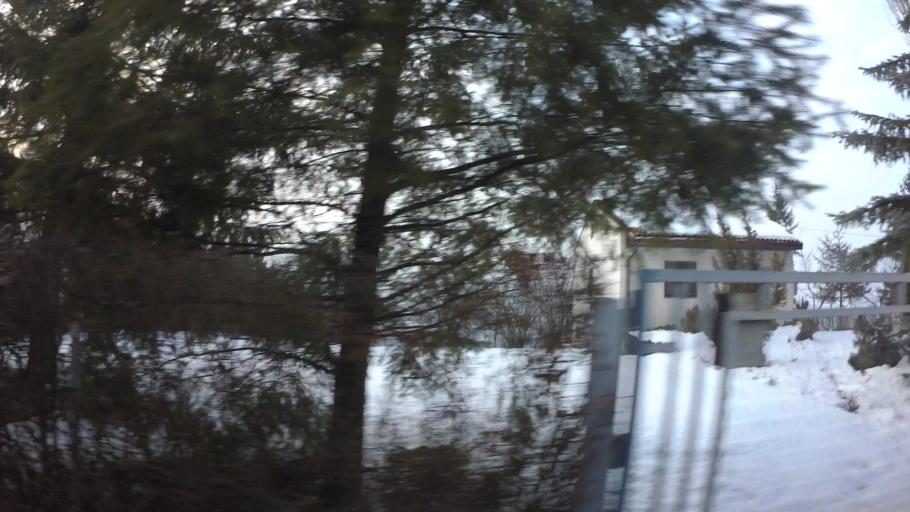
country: BA
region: Federation of Bosnia and Herzegovina
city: Hotonj
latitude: 43.8921
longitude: 18.3671
